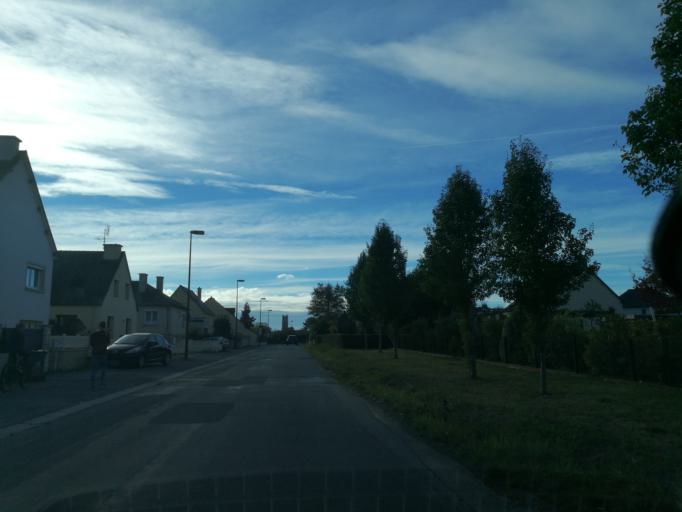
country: FR
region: Brittany
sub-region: Departement d'Ille-et-Vilaine
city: Montauban-de-Bretagne
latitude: 48.1993
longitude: -2.0400
